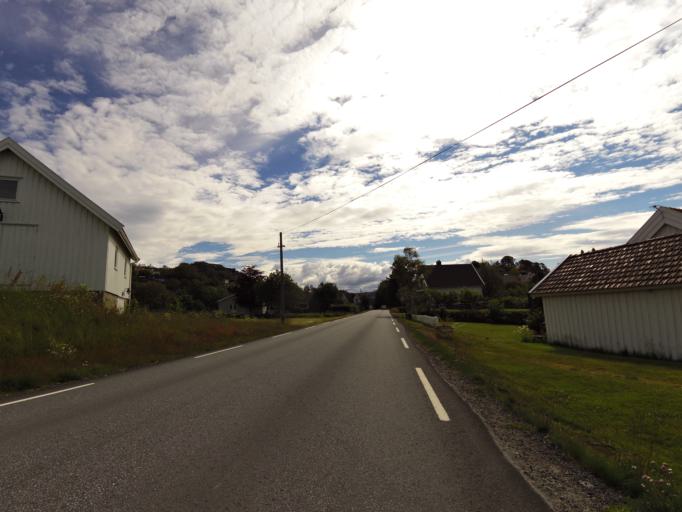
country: NO
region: Vest-Agder
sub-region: Lyngdal
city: Lyngdal
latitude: 58.0459
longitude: 7.1556
